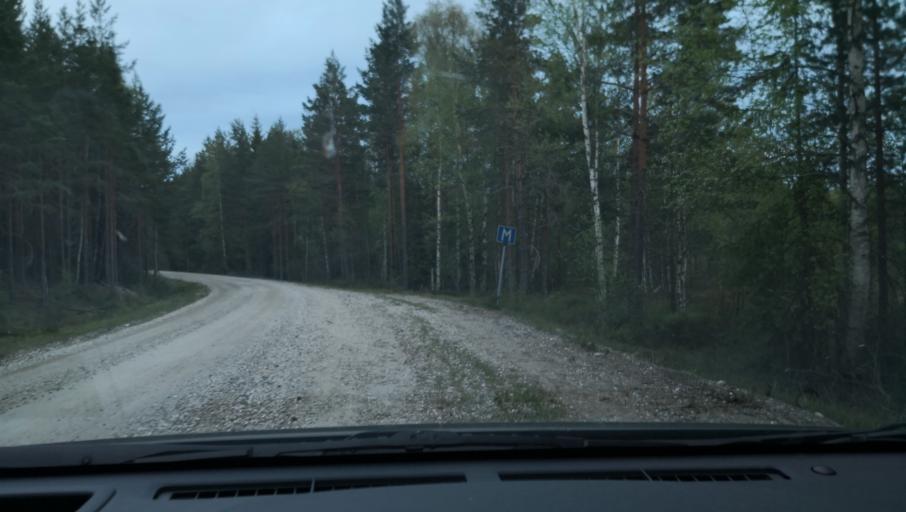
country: SE
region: Vaestmanland
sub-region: Skinnskattebergs Kommun
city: Skinnskatteberg
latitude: 59.7606
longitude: 15.4593
